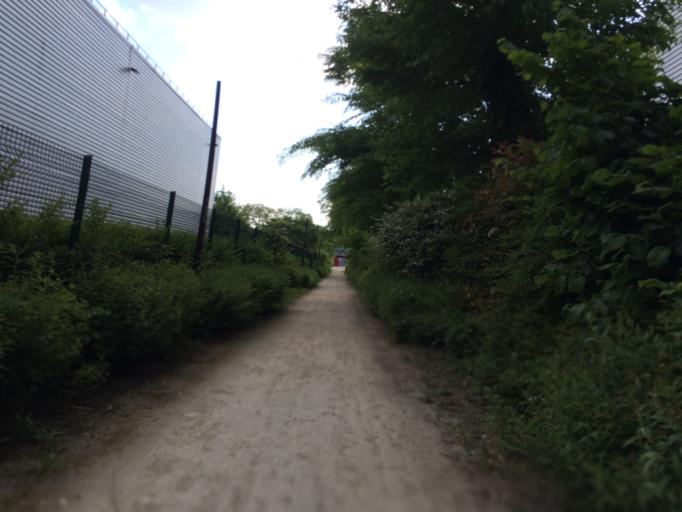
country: FR
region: Ile-de-France
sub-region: Departement de l'Essonne
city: Grigny
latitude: 48.6424
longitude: 2.3956
